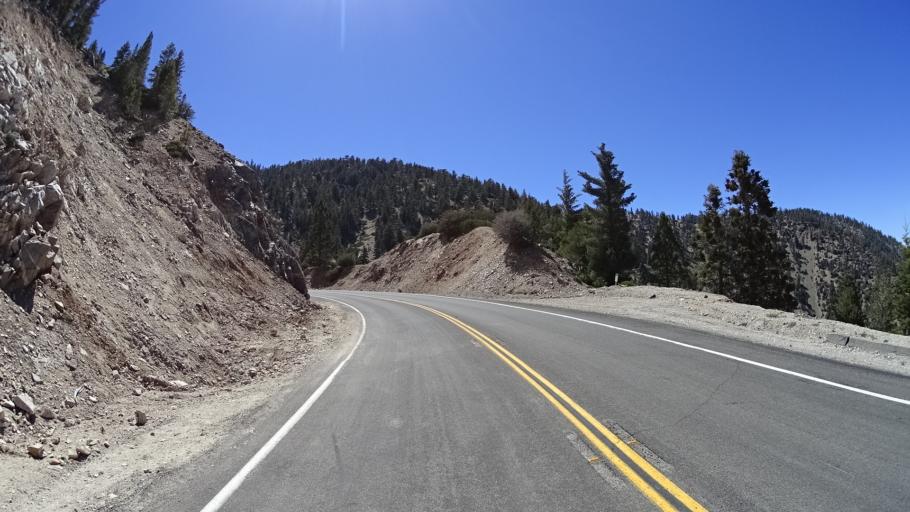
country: US
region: California
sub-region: San Bernardino County
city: Wrightwood
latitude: 34.3594
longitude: -117.7951
